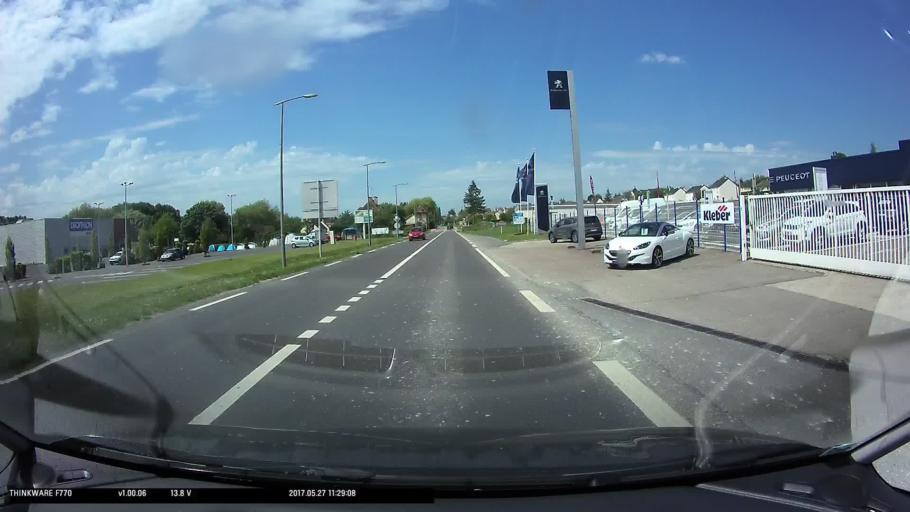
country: FR
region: Haute-Normandie
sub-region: Departement de l'Eure
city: Gisors
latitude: 49.2874
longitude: 1.8002
